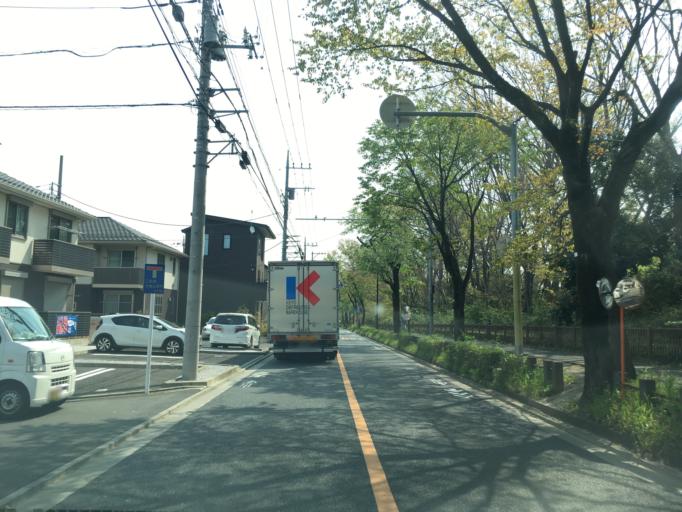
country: JP
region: Tokyo
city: Kokubunji
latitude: 35.7126
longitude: 139.5035
